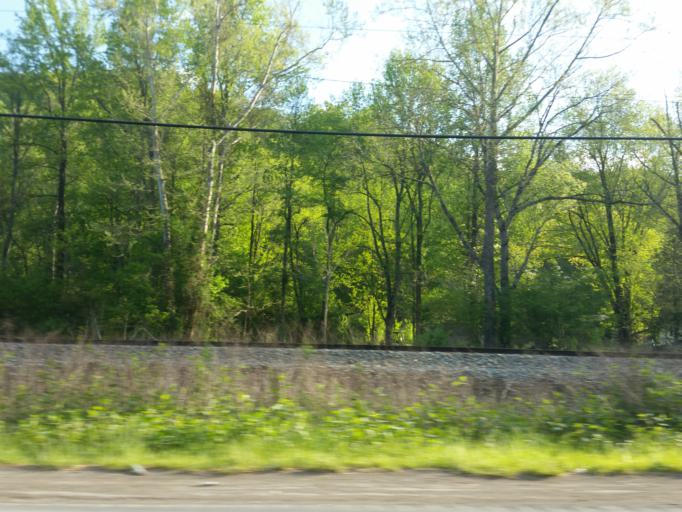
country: US
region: Kentucky
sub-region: Bell County
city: Middlesboro
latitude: 36.6143
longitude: -83.7641
